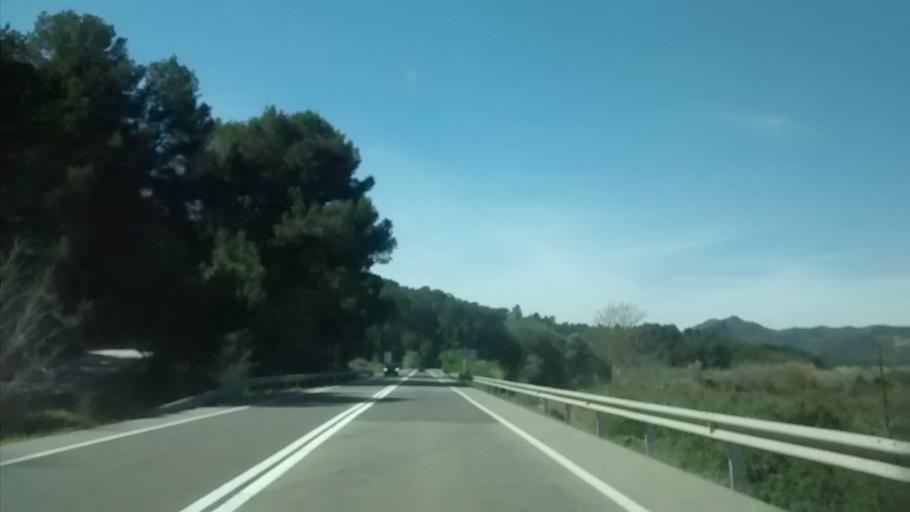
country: ES
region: Catalonia
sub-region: Provincia de Tarragona
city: Ginestar
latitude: 41.0350
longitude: 0.6267
